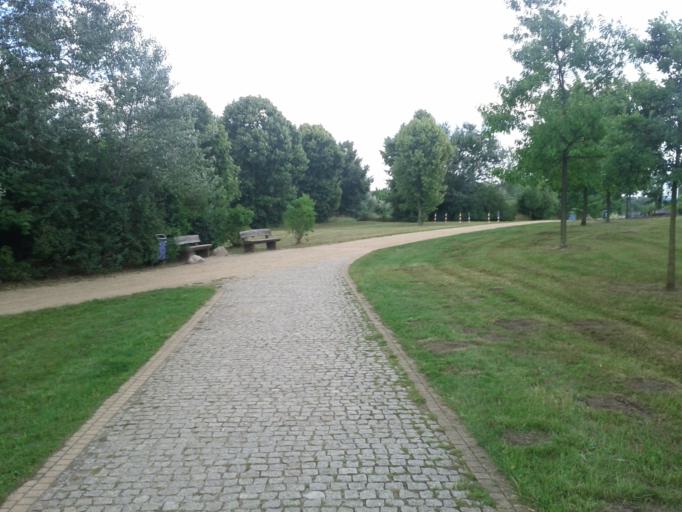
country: DE
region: Brandenburg
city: Ahrensfelde
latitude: 52.5647
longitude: 13.5816
